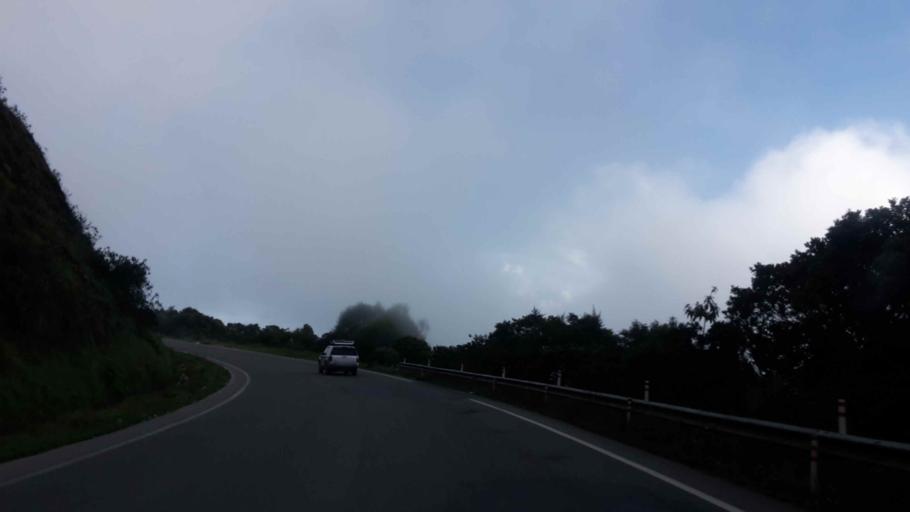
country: BO
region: Cochabamba
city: Colomi
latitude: -17.2197
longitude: -65.8933
